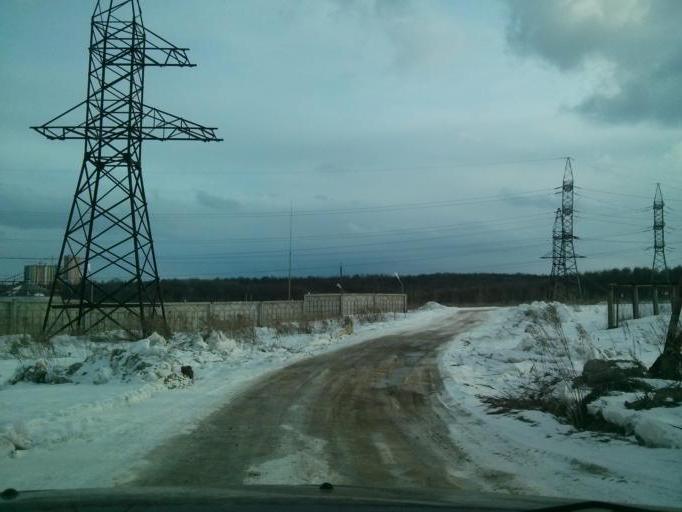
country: RU
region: Nizjnij Novgorod
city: Afonino
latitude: 56.2645
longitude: 44.0312
